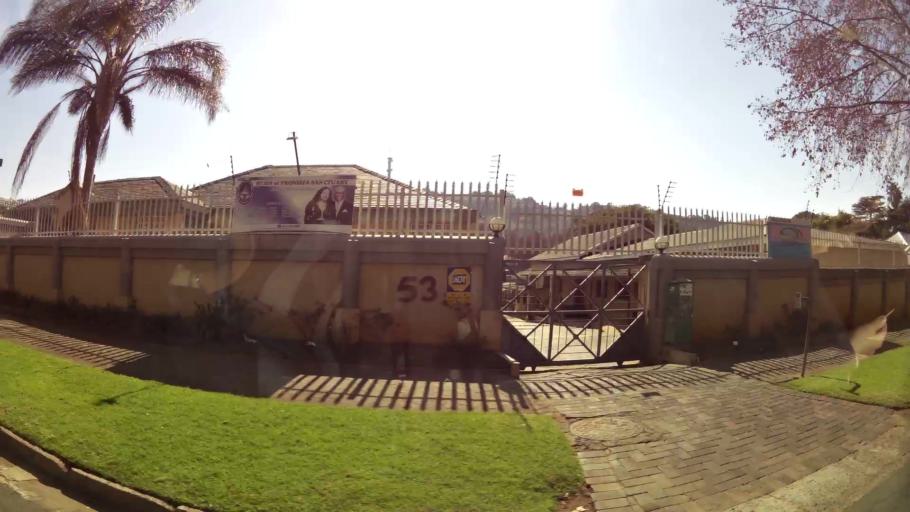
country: ZA
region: Gauteng
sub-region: City of Johannesburg Metropolitan Municipality
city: Johannesburg
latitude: -26.1901
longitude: 28.0794
